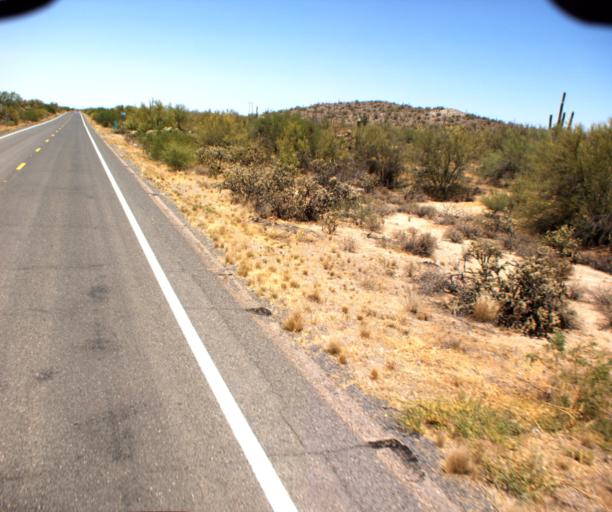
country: US
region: Arizona
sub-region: Pinal County
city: Florence
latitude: 32.7798
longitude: -111.1659
